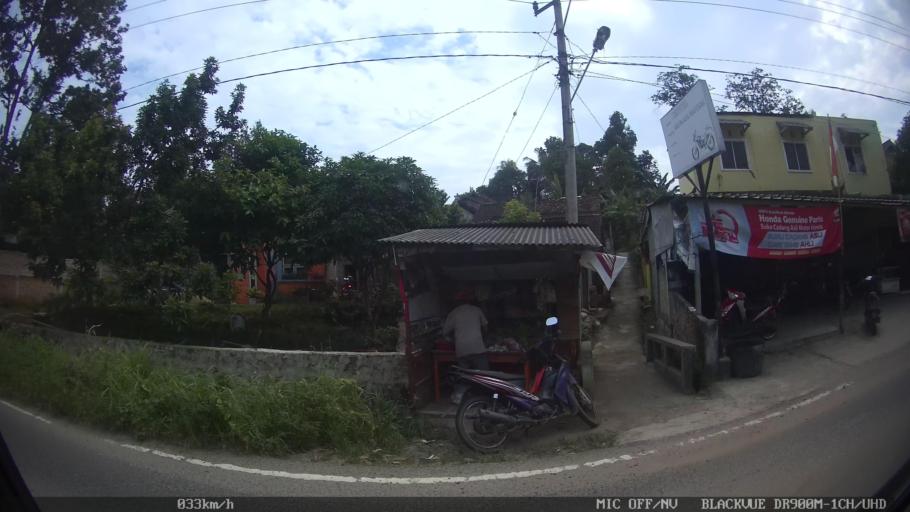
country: ID
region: Lampung
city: Bandarlampung
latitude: -5.4420
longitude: 105.2411
